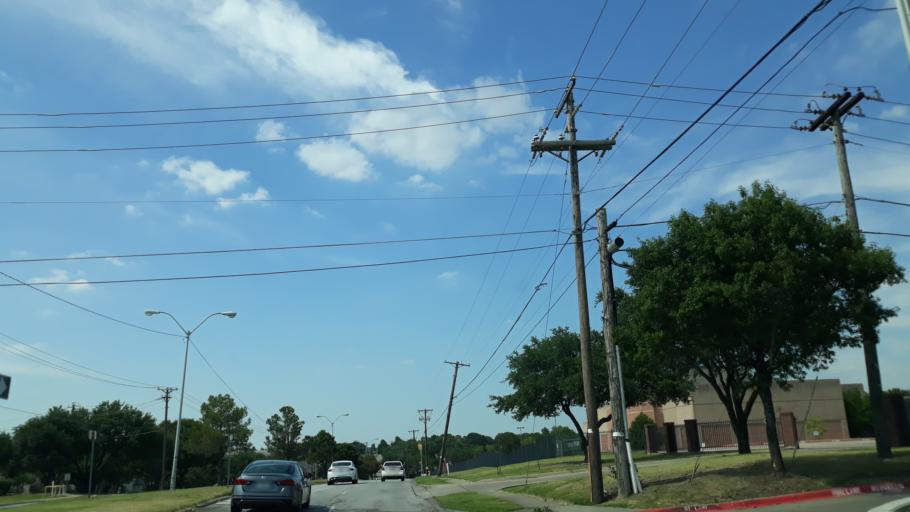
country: US
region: Texas
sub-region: Dallas County
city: Irving
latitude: 32.8384
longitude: -97.0095
